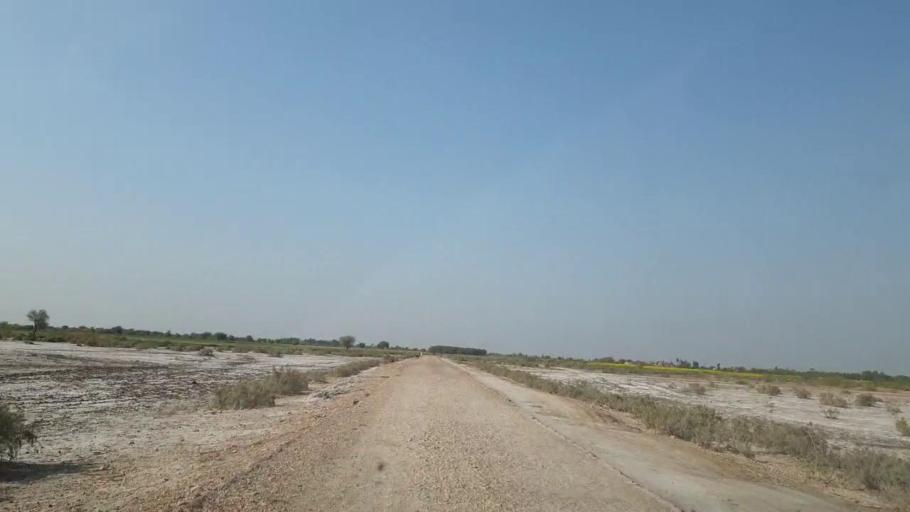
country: PK
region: Sindh
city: Tando Mittha Khan
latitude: 25.7578
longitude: 69.1950
